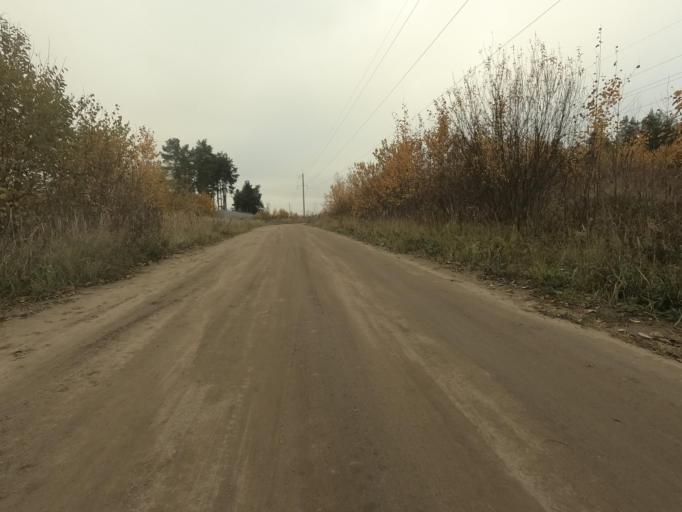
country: RU
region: Leningrad
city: Kirovsk
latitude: 59.8536
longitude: 30.9848
